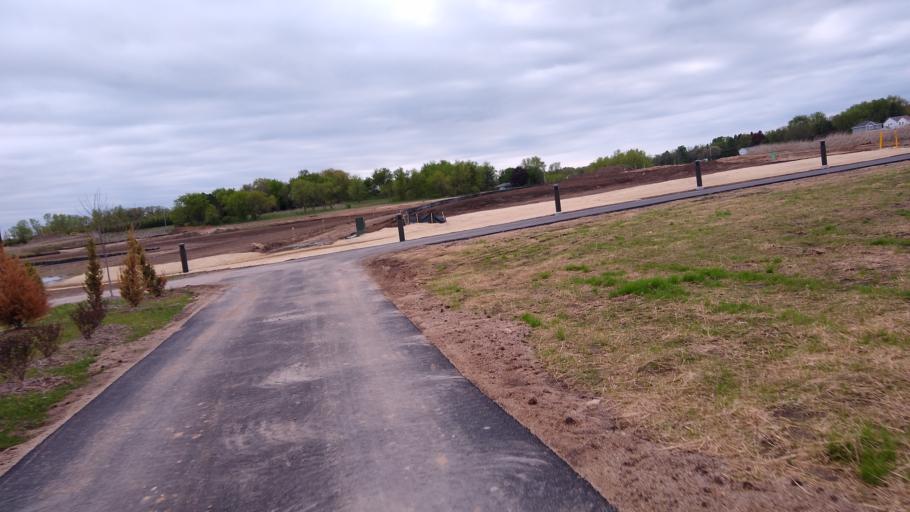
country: US
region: Wisconsin
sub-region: Dane County
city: Monona
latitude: 43.0095
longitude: -89.3700
